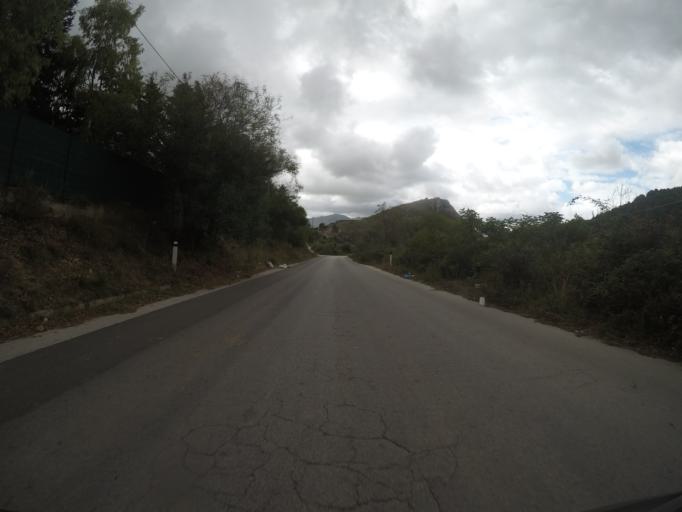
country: IT
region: Sicily
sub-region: Palermo
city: Montelepre
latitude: 38.1031
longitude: 13.1712
